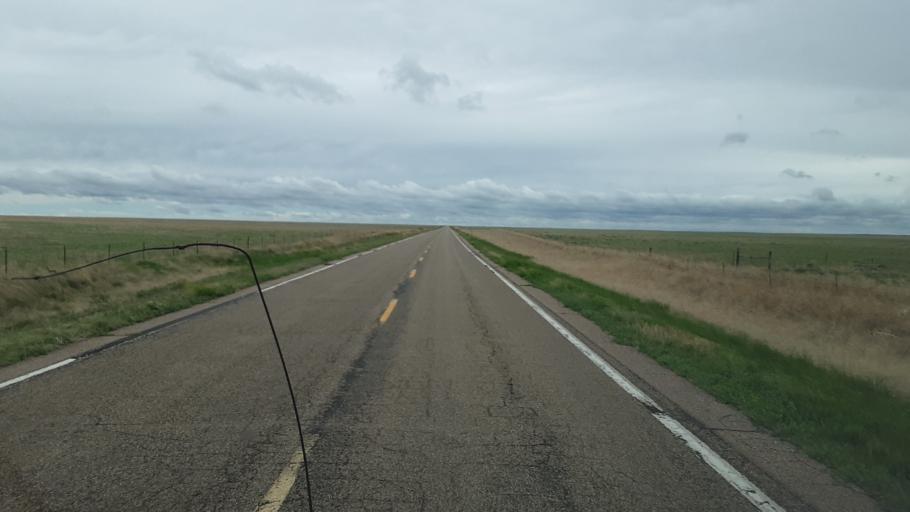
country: US
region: Colorado
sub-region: Lincoln County
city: Hugo
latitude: 38.8521
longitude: -103.7372
